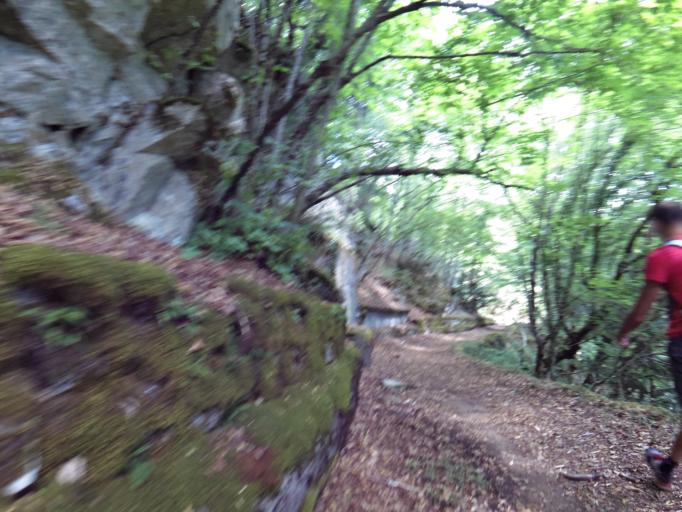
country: IT
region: Calabria
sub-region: Provincia di Vibo-Valentia
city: Nardodipace
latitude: 38.5072
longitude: 16.3841
